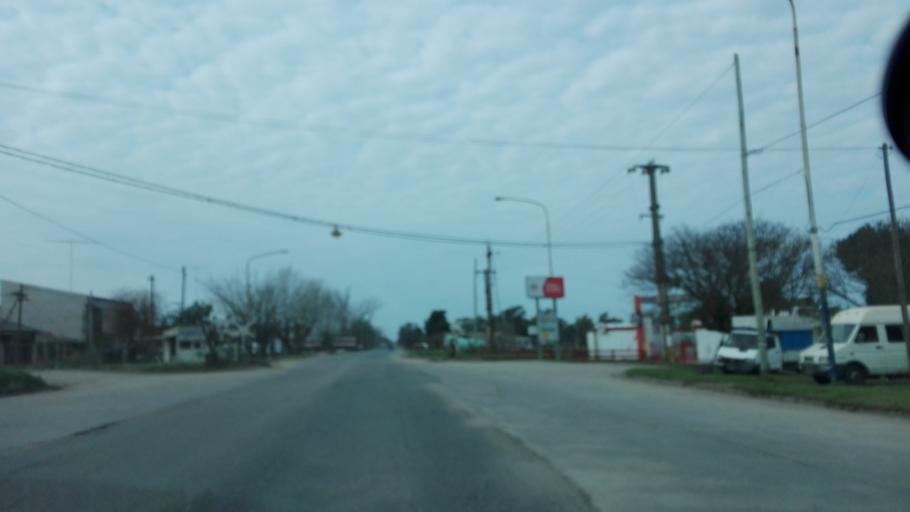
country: AR
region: Buenos Aires
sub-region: Partido de Chascomus
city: Chascomus
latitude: -35.5759
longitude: -57.9992
